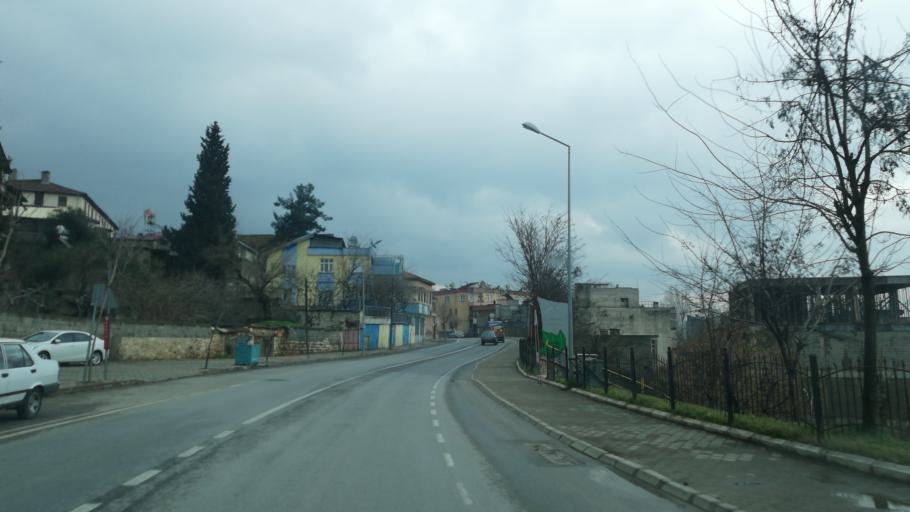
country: TR
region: Kahramanmaras
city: Kahramanmaras
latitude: 37.5929
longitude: 36.9310
